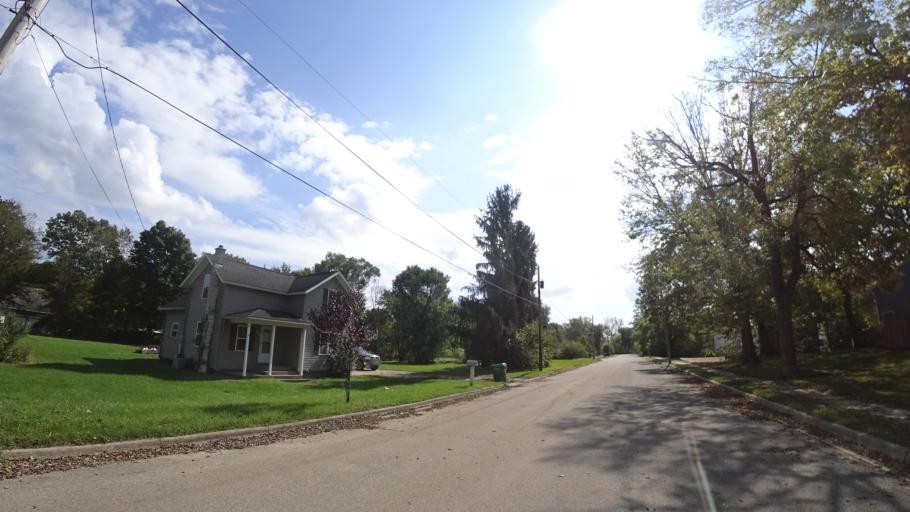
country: US
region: Michigan
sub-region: Saint Joseph County
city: Three Rivers
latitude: 41.9291
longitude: -85.6297
